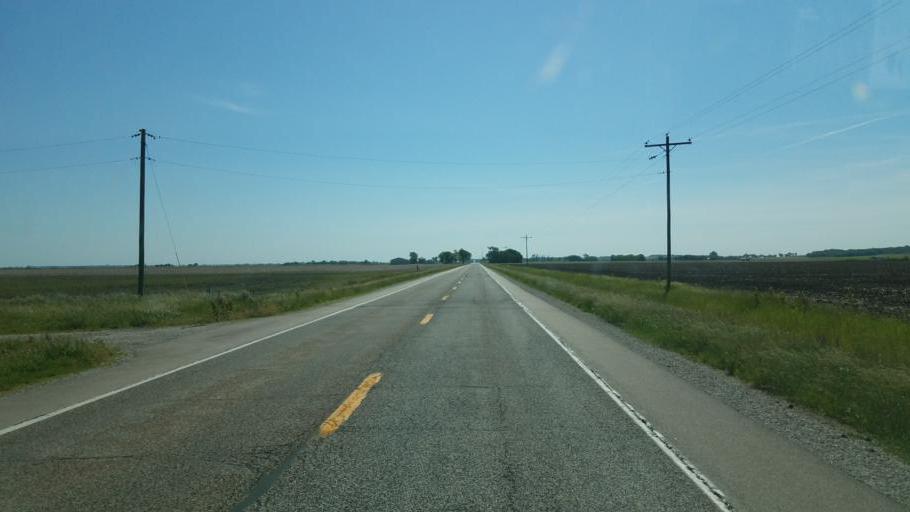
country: US
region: Illinois
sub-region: Mason County
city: Mason City
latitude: 40.3047
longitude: -89.7086
